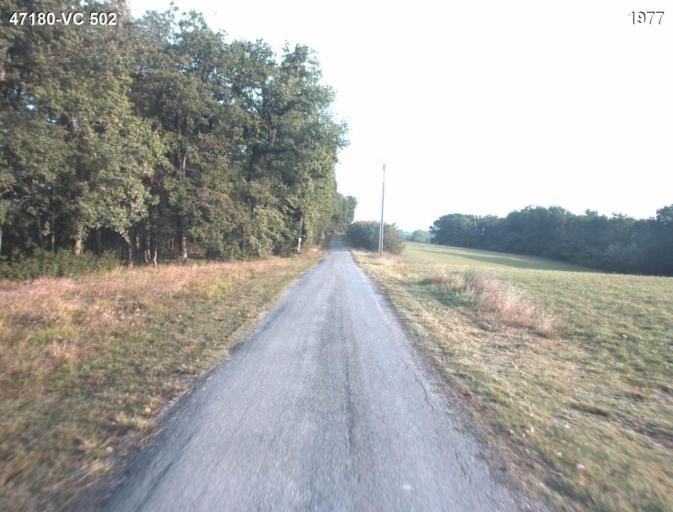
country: FR
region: Aquitaine
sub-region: Departement du Lot-et-Garonne
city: Sainte-Colombe-en-Bruilhois
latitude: 44.1746
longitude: 0.4826
